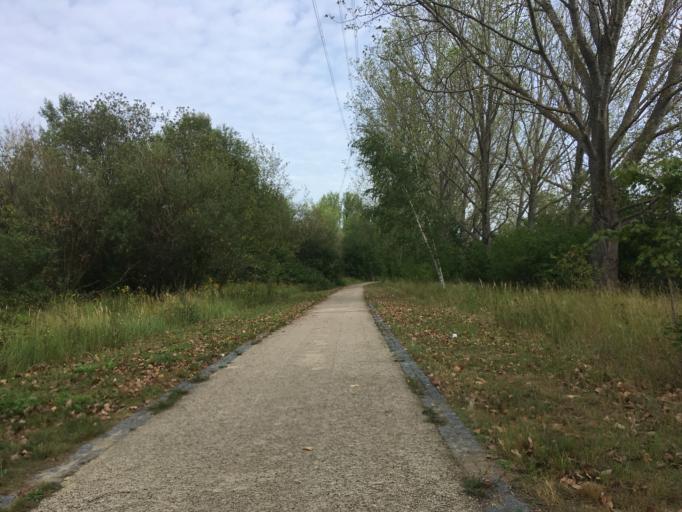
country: DE
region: Berlin
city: Falkenberg
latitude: 52.5565
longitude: 13.5427
